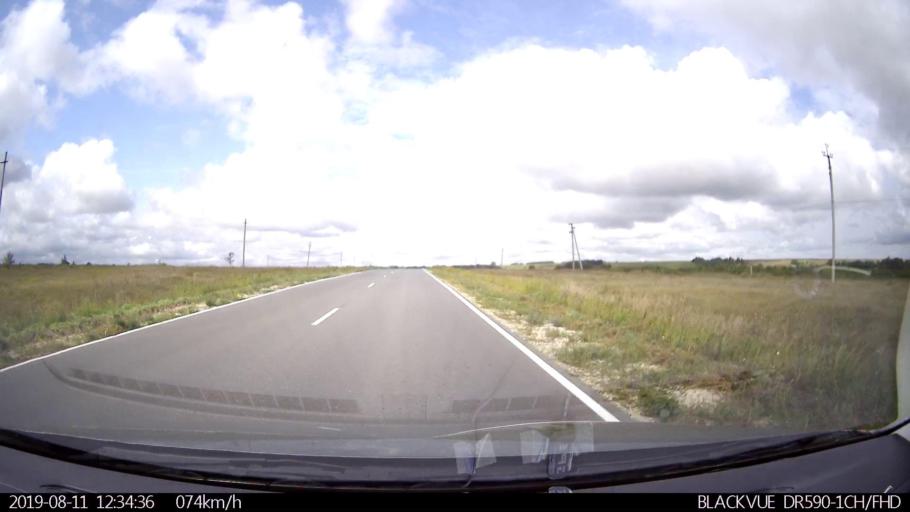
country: RU
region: Ulyanovsk
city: Ignatovka
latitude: 53.8181
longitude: 47.8405
